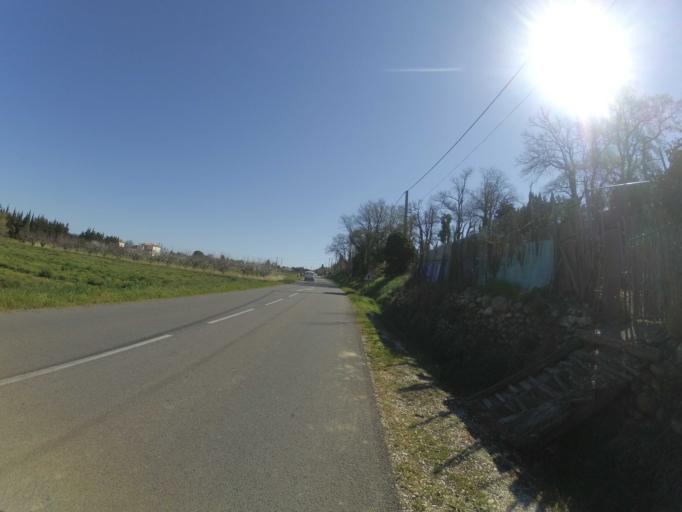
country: FR
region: Languedoc-Roussillon
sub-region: Departement des Pyrenees-Orientales
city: Ille-sur-Tet
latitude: 42.6556
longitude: 2.6186
